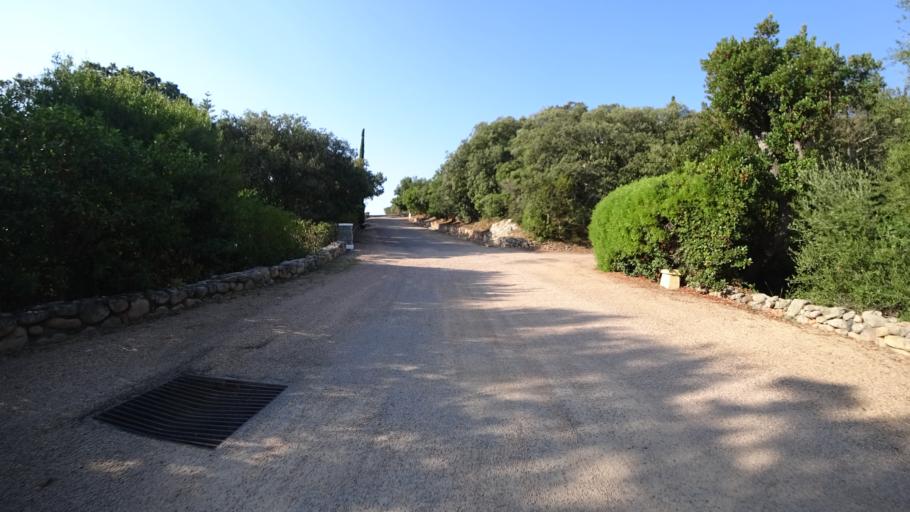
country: FR
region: Corsica
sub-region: Departement de la Corse-du-Sud
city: Porto-Vecchio
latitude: 41.6224
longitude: 9.3527
